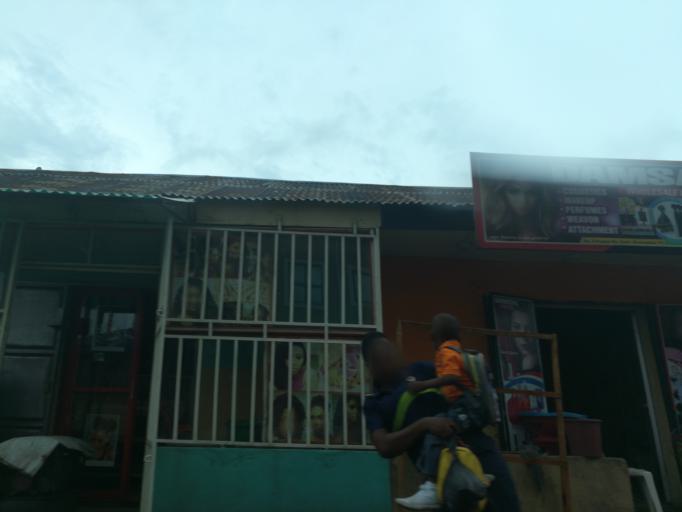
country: NG
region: Rivers
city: Port Harcourt
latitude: 4.8541
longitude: 7.0349
